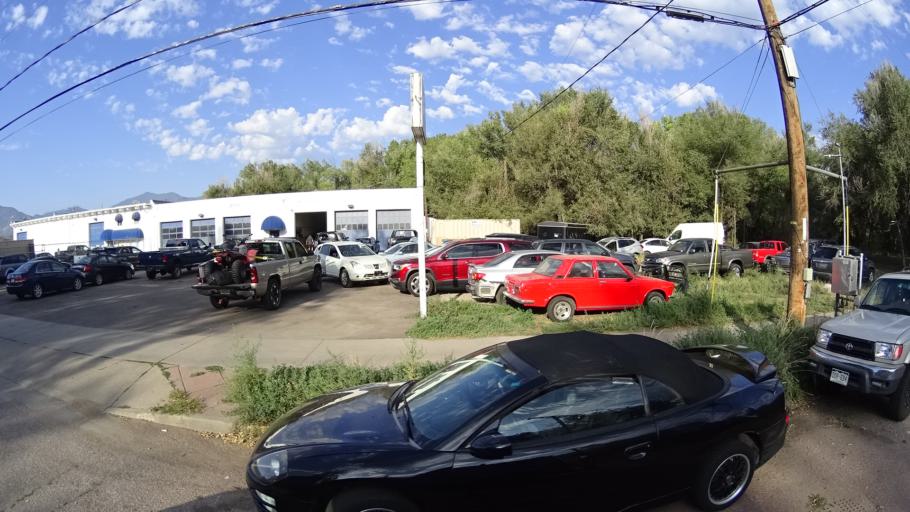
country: US
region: Colorado
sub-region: El Paso County
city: Colorado Springs
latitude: 38.8314
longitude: -104.8134
